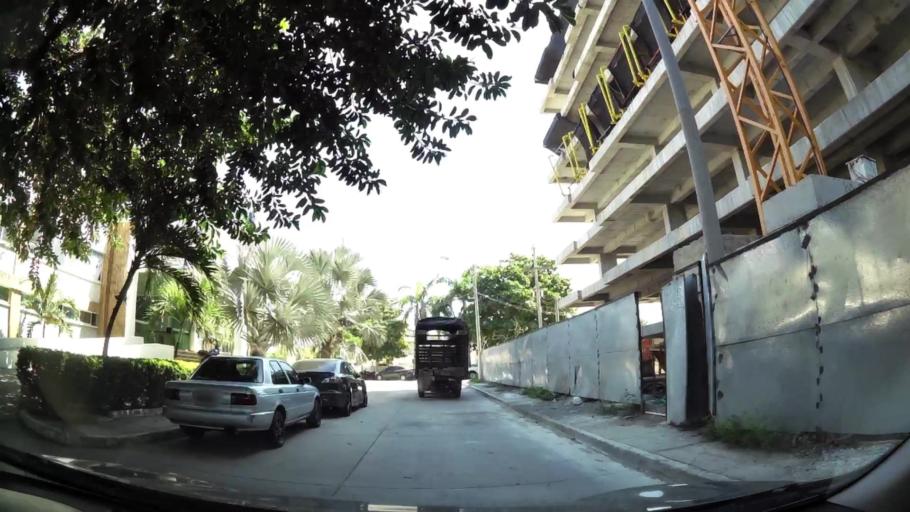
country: CO
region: Bolivar
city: Cartagena
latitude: 10.4521
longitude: -75.5146
